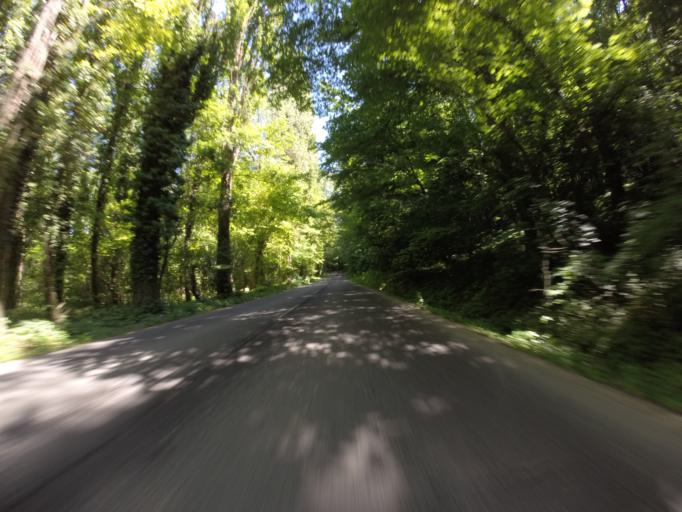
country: SK
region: Trnavsky
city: Hlohovec
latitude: 48.4608
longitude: 17.8309
